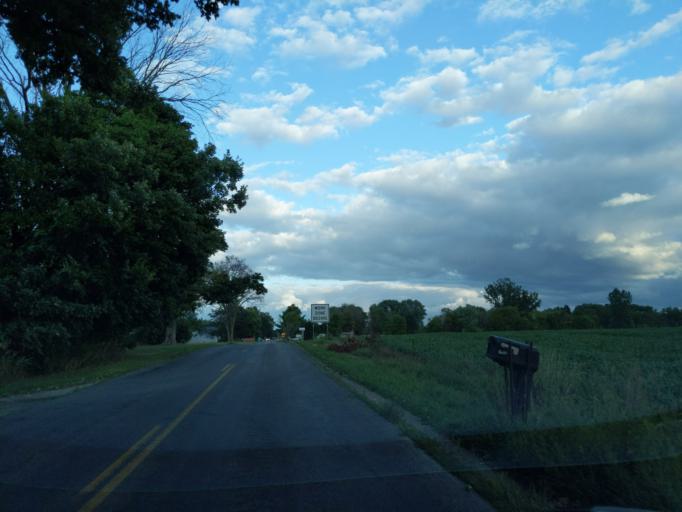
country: US
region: Michigan
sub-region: Ingham County
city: Holt
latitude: 42.5968
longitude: -84.5473
